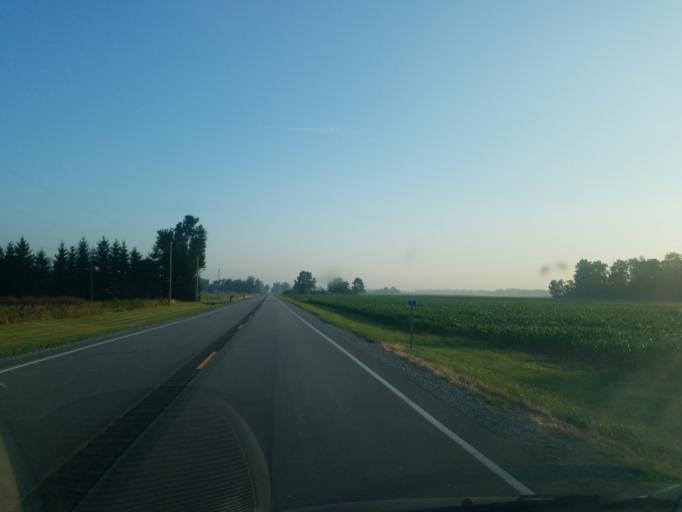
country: US
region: Indiana
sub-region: Allen County
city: Harlan
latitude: 41.2205
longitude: -84.8654
